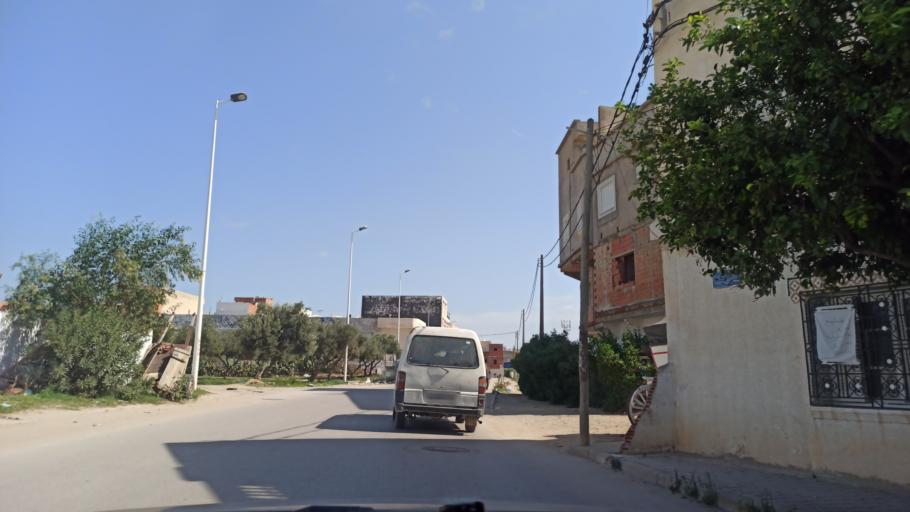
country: TN
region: Nabul
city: Nabeul
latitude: 36.4652
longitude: 10.7368
